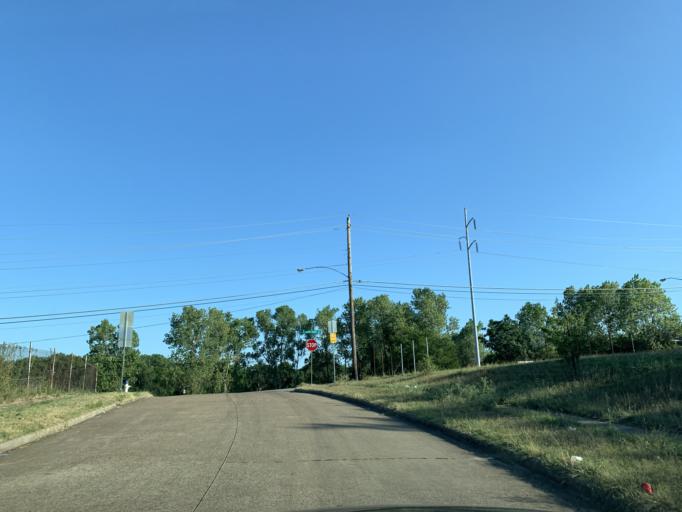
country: US
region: Texas
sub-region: Dallas County
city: Hutchins
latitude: 32.6656
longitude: -96.7785
